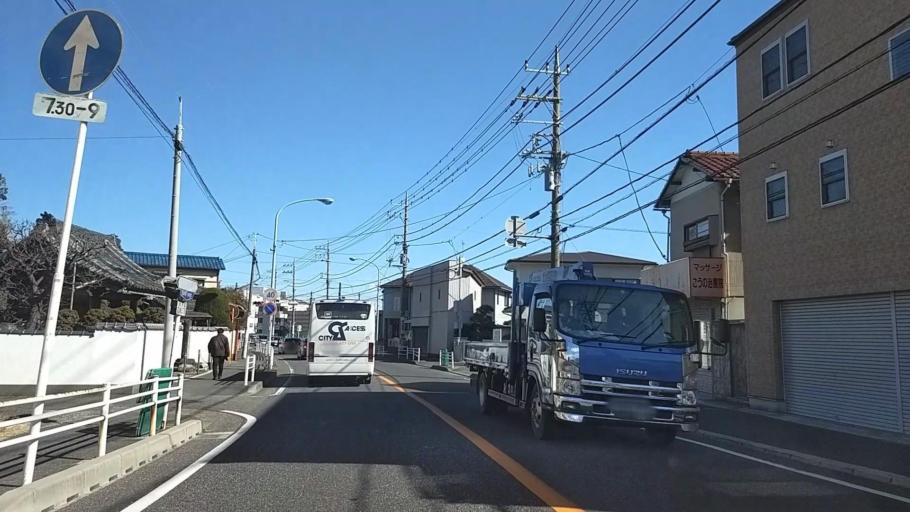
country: JP
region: Kanagawa
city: Zushi
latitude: 35.3272
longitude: 139.6119
